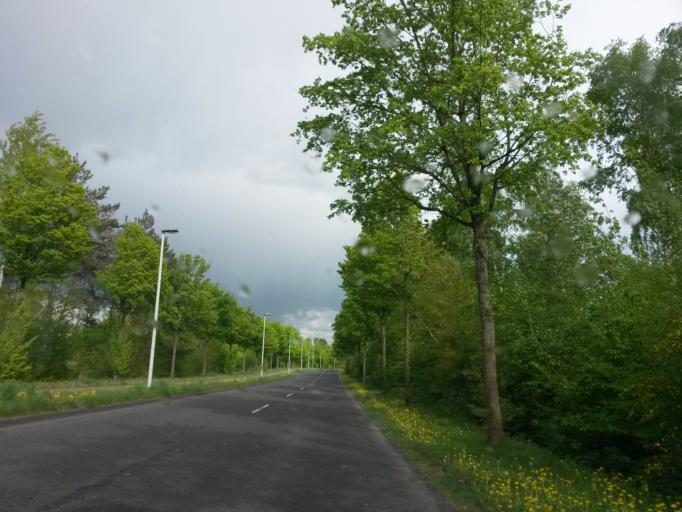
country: DE
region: North Rhine-Westphalia
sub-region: Regierungsbezirk Koln
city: Alfter
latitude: 50.6958
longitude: 7.0429
